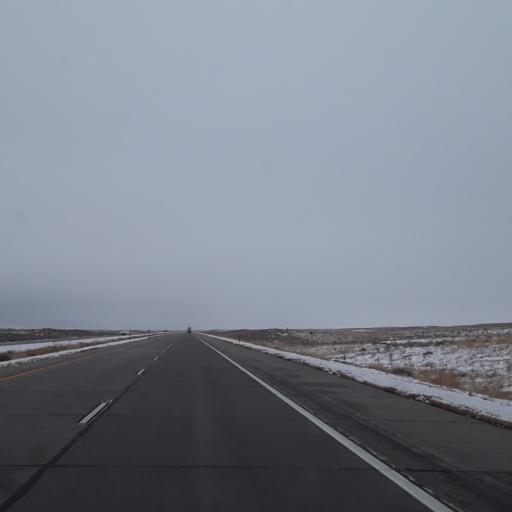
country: US
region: Colorado
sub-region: Logan County
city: Sterling
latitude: 40.5502
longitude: -103.2178
